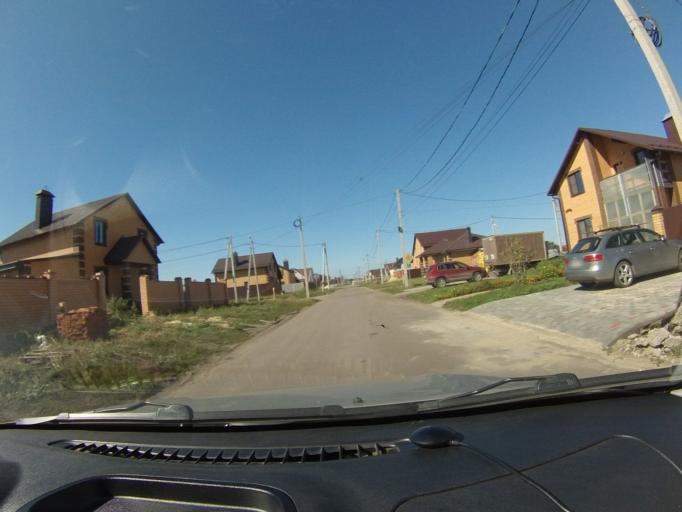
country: RU
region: Tambov
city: Tambov
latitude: 52.7746
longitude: 41.3739
